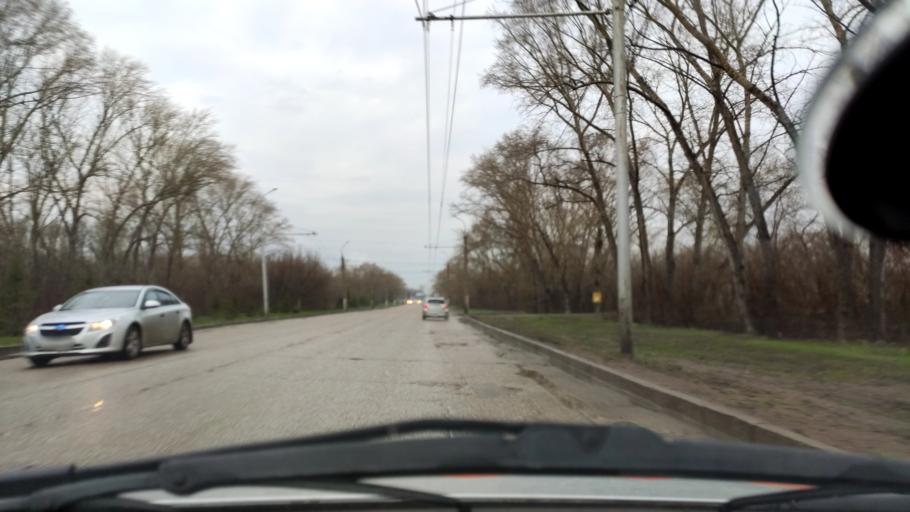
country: RU
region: Bashkortostan
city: Sterlitamak
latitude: 53.6584
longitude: 55.9488
